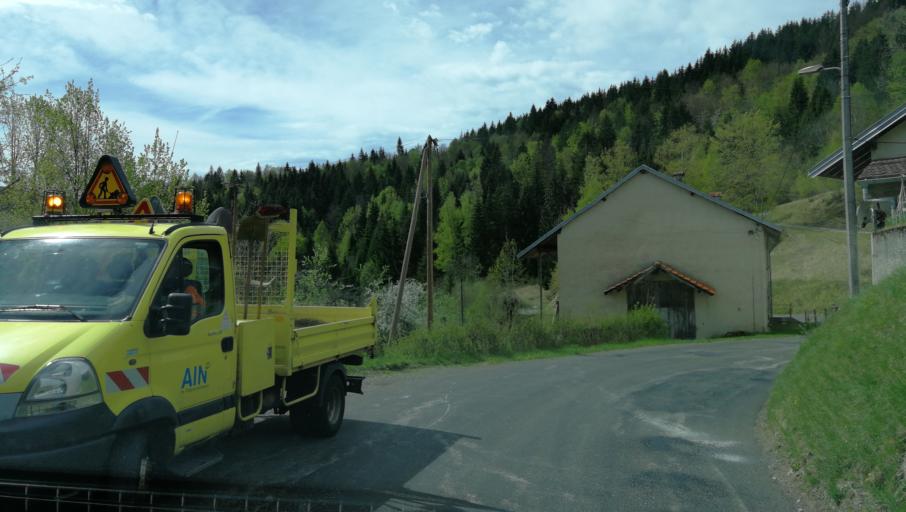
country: FR
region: Rhone-Alpes
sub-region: Departement de l'Ain
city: Oyonnax
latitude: 46.2244
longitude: 5.7444
